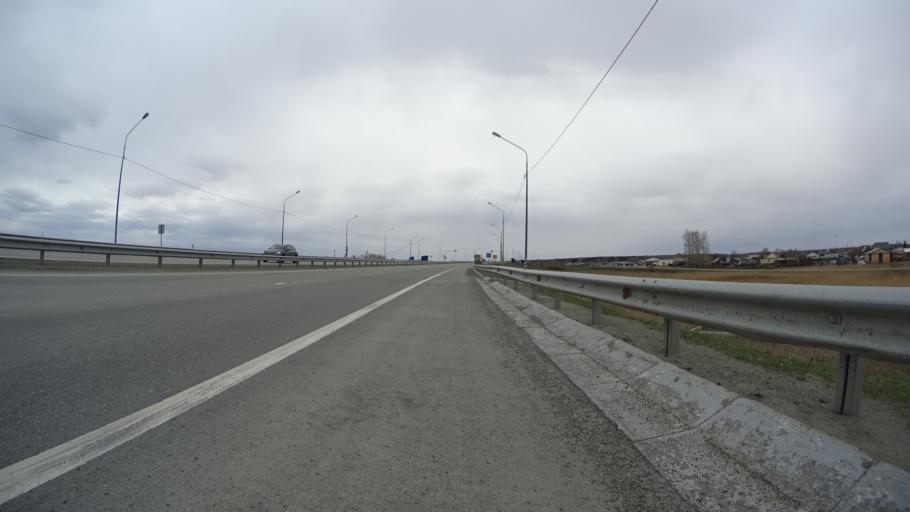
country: RU
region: Chelyabinsk
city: Yemanzhelinka
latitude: 54.7984
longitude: 61.3083
